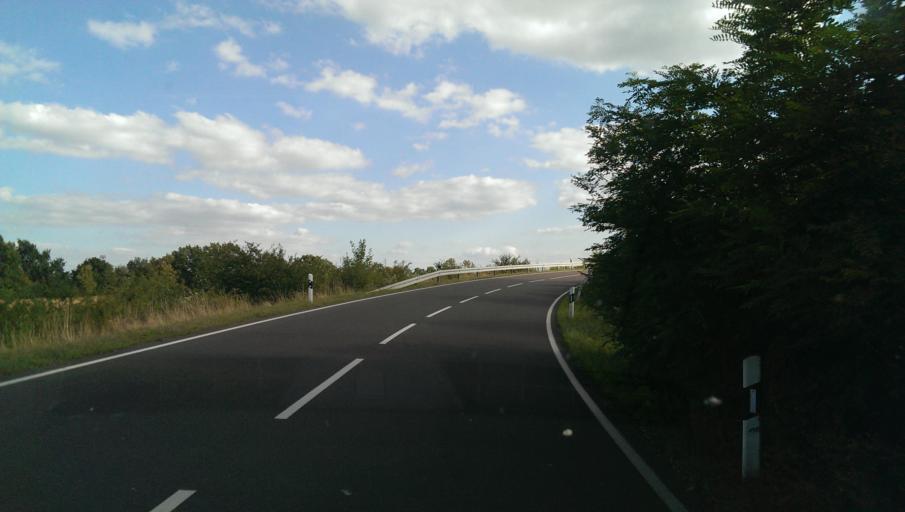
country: DE
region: Saxony
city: Rackwitz
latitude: 51.4186
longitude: 12.3815
